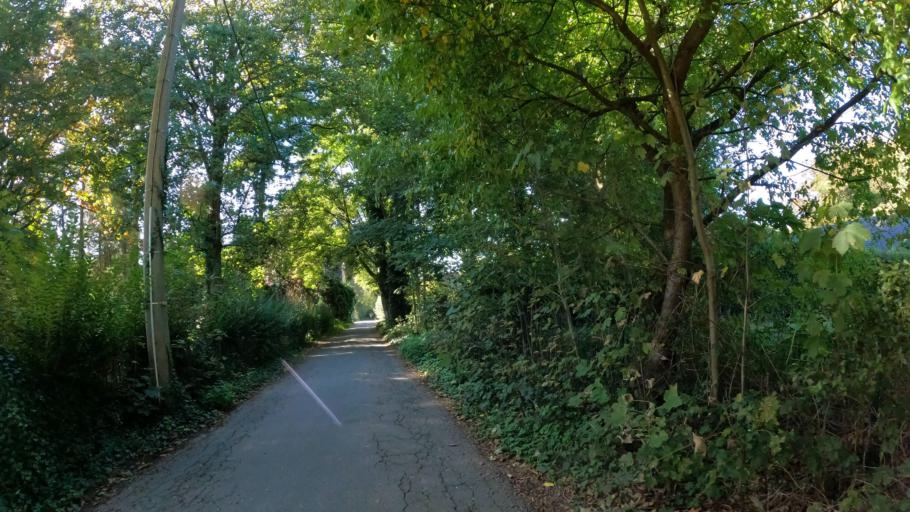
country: BE
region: Flanders
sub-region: Provincie Oost-Vlaanderen
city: Waasmunster
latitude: 51.1204
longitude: 4.0996
